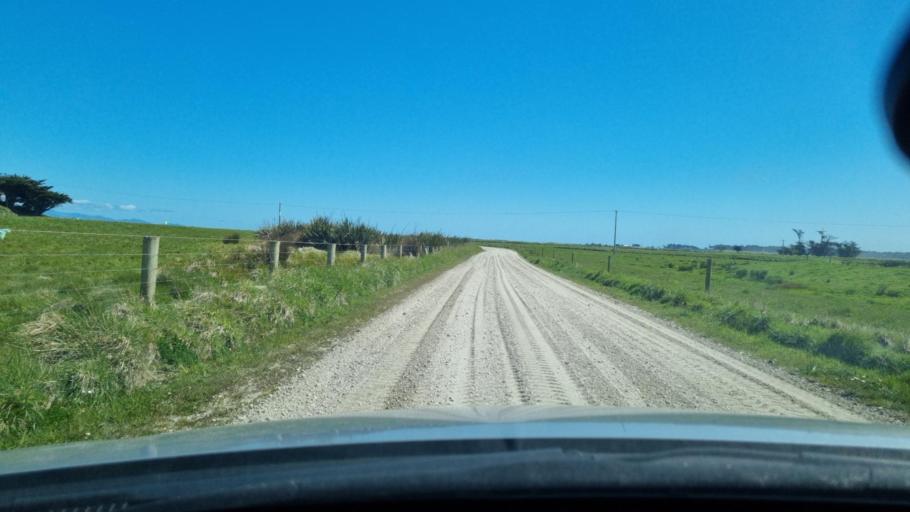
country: NZ
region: Southland
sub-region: Invercargill City
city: Invercargill
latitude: -46.3915
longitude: 168.2602
